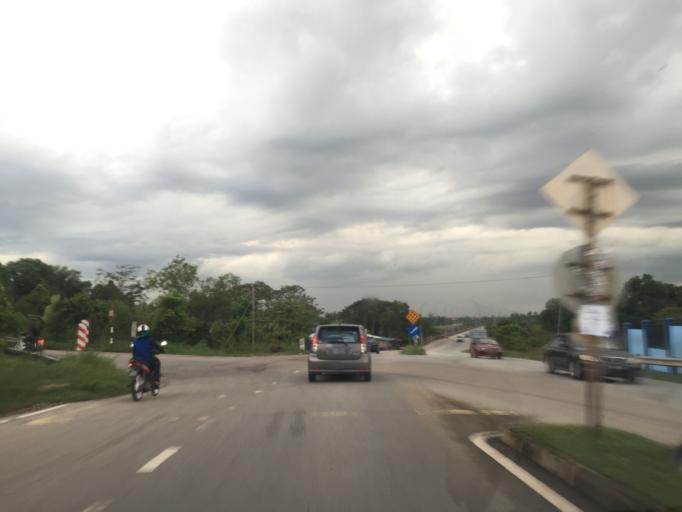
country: MY
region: Kedah
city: Sungai Petani
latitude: 5.5694
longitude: 100.5040
